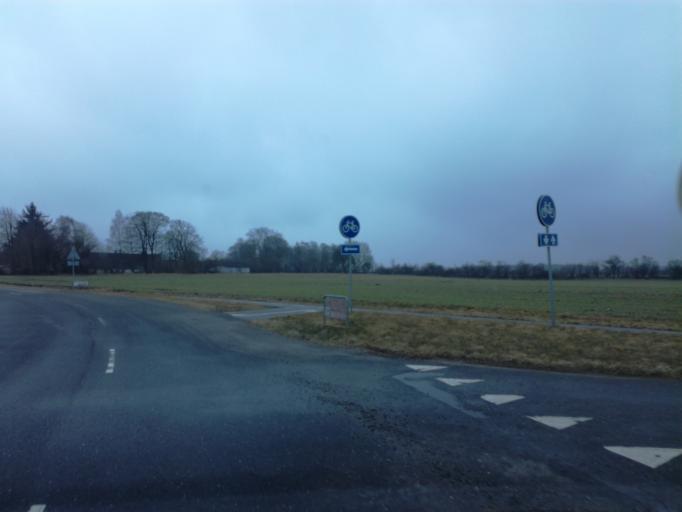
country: DK
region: South Denmark
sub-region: Vejle Kommune
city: Borkop
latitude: 55.6284
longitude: 9.5838
